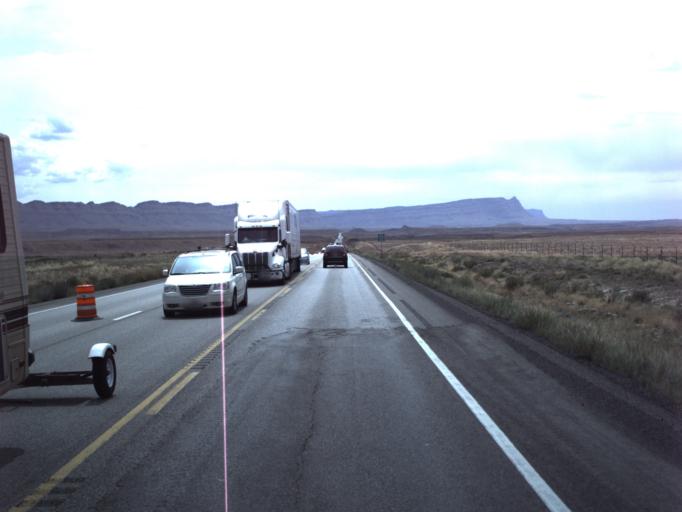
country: US
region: Utah
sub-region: Carbon County
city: East Carbon City
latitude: 39.3880
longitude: -110.4125
